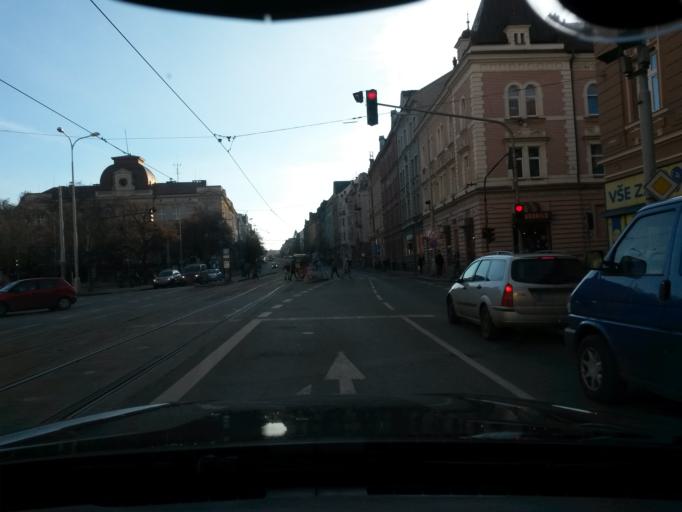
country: CZ
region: Plzensky
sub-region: Okres Plzen-Mesto
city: Pilsen
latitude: 49.7383
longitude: 13.3707
